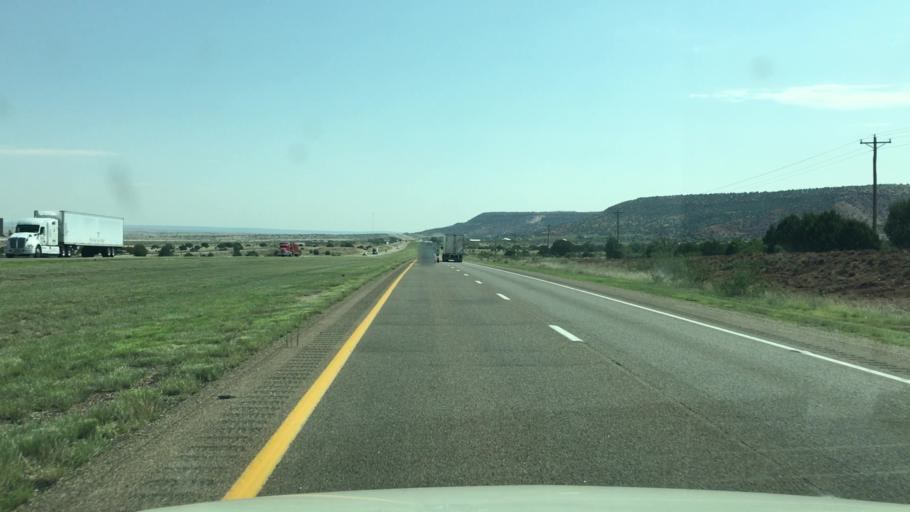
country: US
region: New Mexico
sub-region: Guadalupe County
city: Santa Rosa
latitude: 35.0238
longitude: -104.4261
